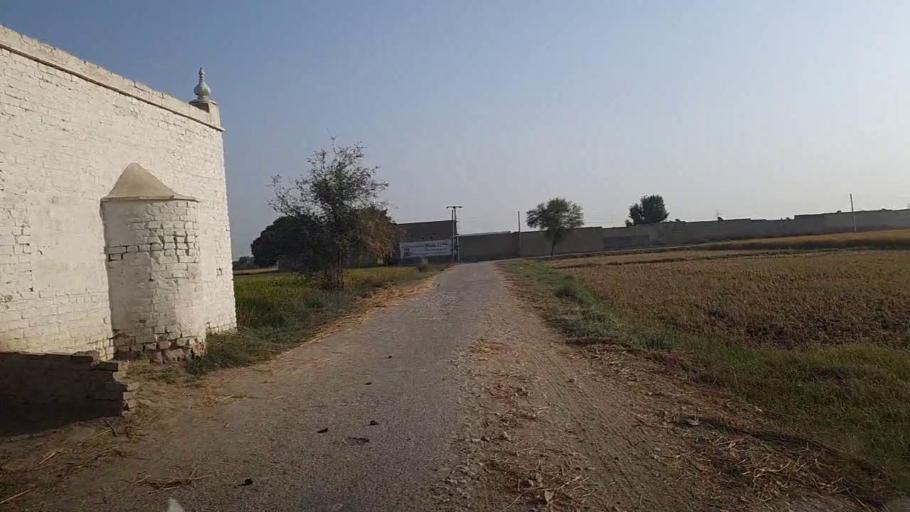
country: PK
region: Sindh
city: Kandhkot
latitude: 28.2521
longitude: 69.1601
